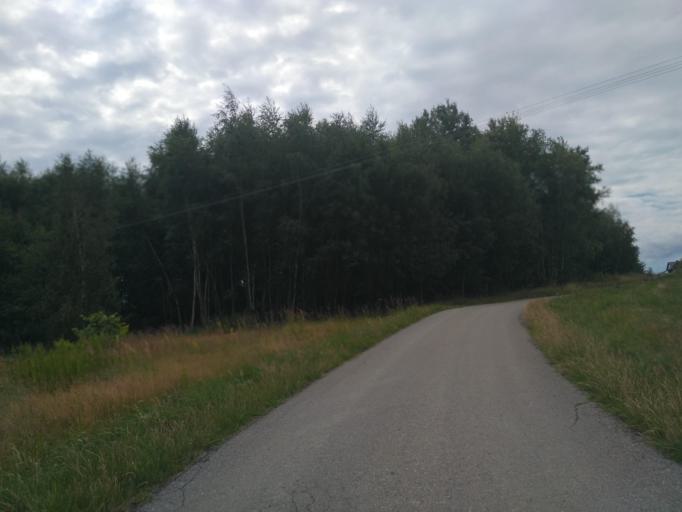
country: PL
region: Subcarpathian Voivodeship
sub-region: Powiat rzeszowski
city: Straszydle
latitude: 49.8903
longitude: 21.9820
